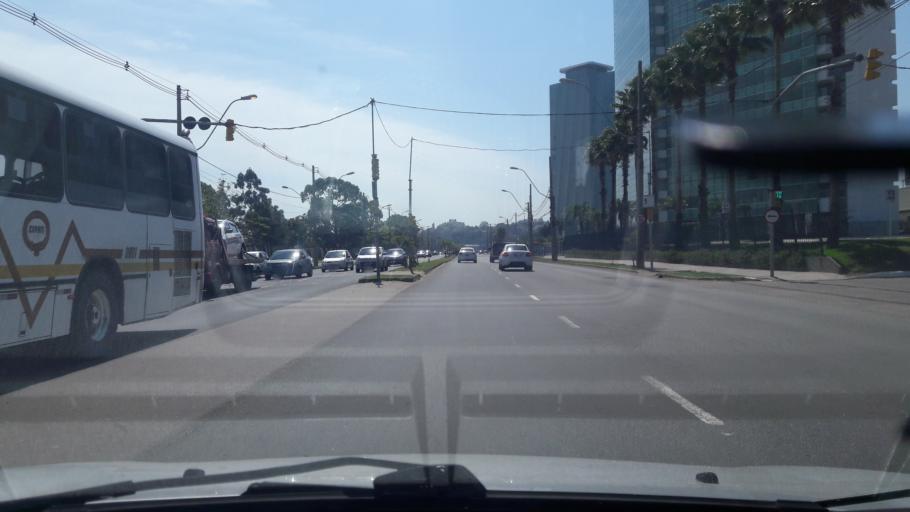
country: BR
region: Rio Grande do Sul
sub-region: Porto Alegre
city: Porto Alegre
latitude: -30.0875
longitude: -51.2480
